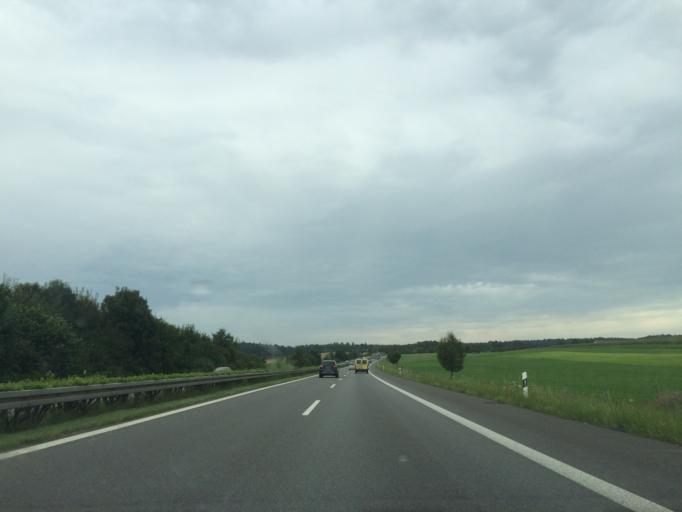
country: DE
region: Baden-Wuerttemberg
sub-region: Tuebingen Region
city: Baindt
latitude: 47.8530
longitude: 9.6420
